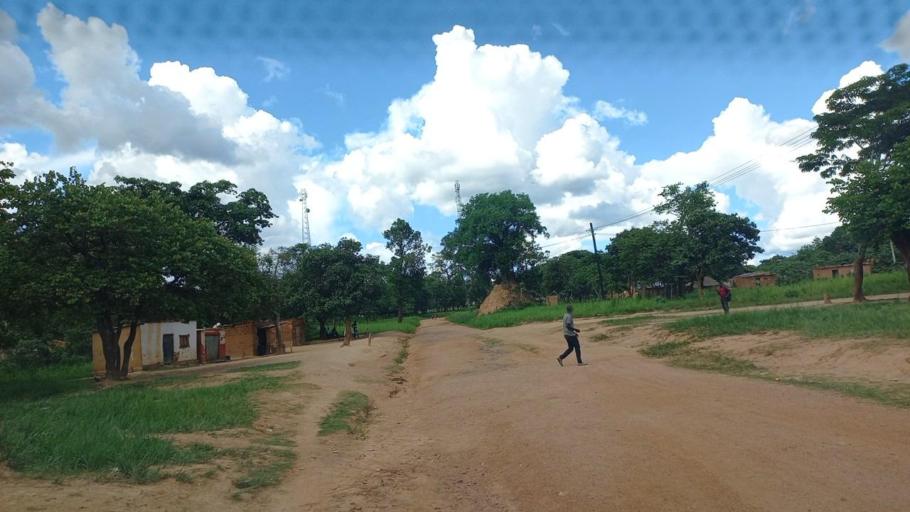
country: ZM
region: North-Western
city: Mwinilunga
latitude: -12.0701
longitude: 24.3012
